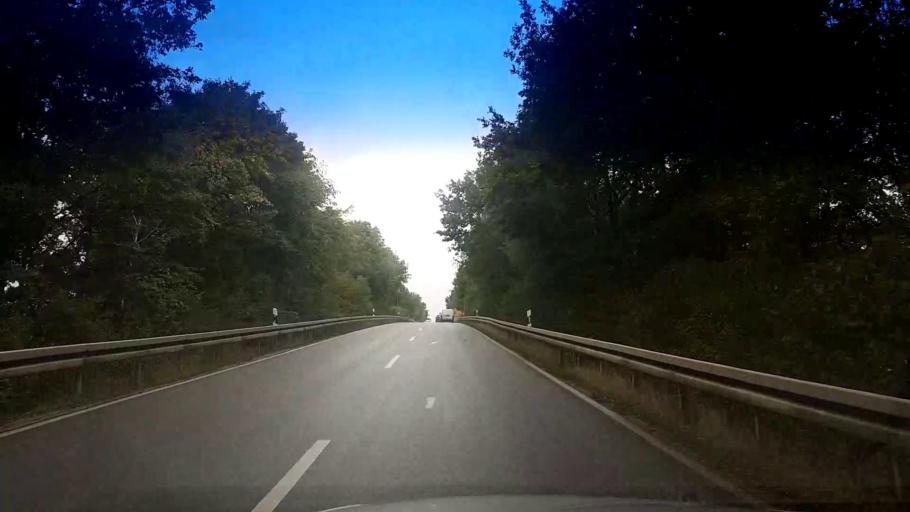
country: DE
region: Bavaria
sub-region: Upper Franconia
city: Eggolsheim
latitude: 49.7726
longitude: 11.0416
